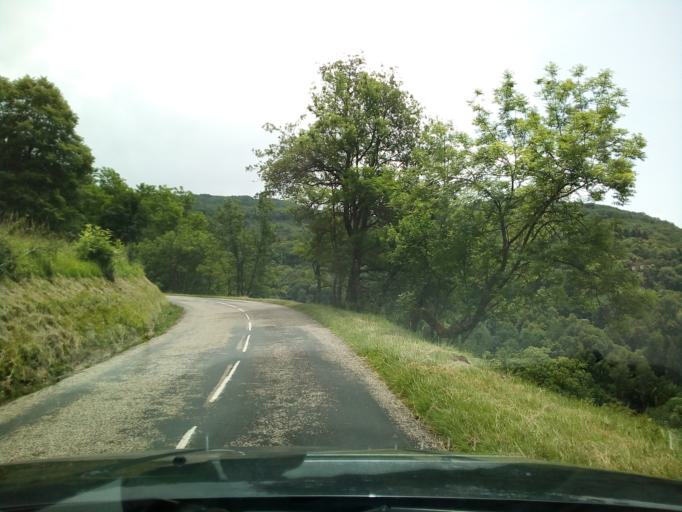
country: FR
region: Rhone-Alpes
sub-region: Departement de l'Isere
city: Saint-Martin-d'Heres
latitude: 45.1645
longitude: 5.7819
